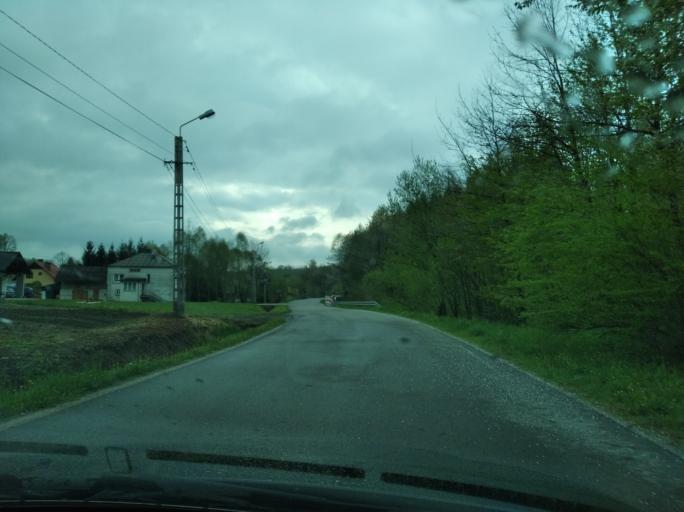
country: PL
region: Subcarpathian Voivodeship
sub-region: Powiat rzeszowski
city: Lecka
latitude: 49.8729
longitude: 22.0231
